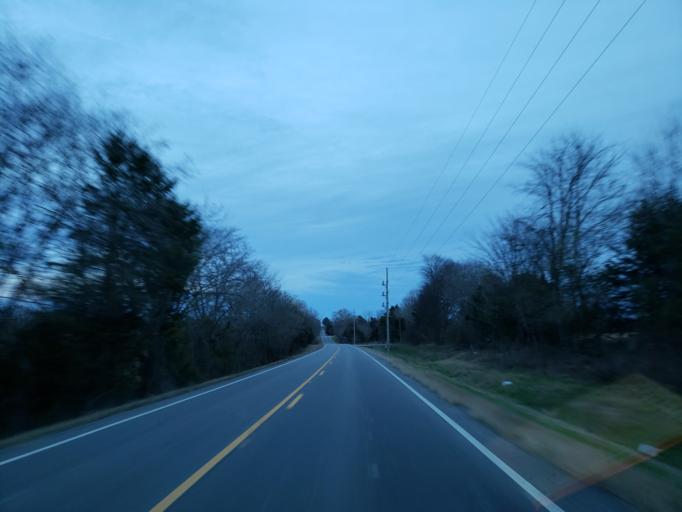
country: US
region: Alabama
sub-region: Sumter County
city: Livingston
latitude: 32.8110
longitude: -88.2662
